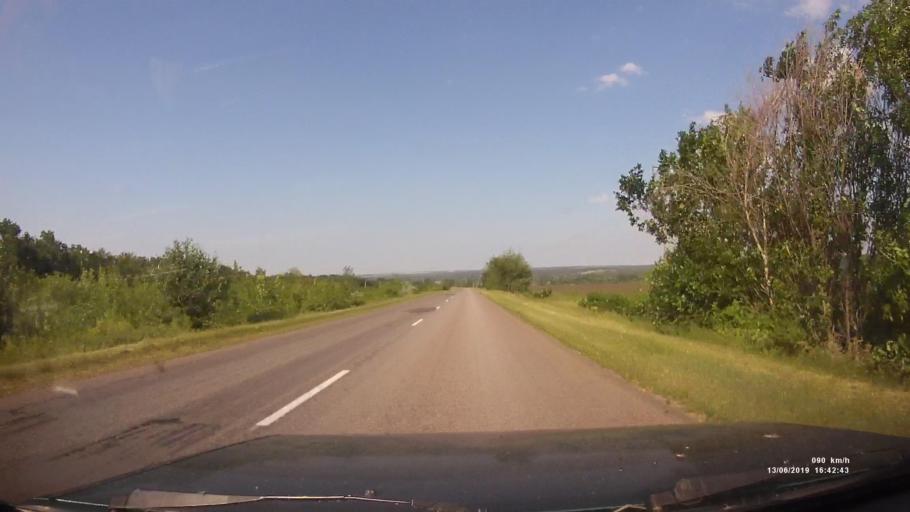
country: RU
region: Rostov
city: Kazanskaya
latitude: 49.9446
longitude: 41.4085
